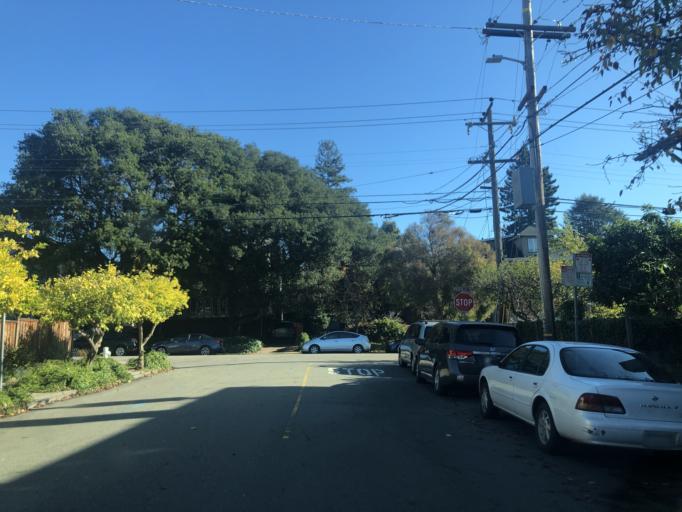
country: US
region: California
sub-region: Alameda County
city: Berkeley
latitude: 37.8588
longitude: -122.2573
